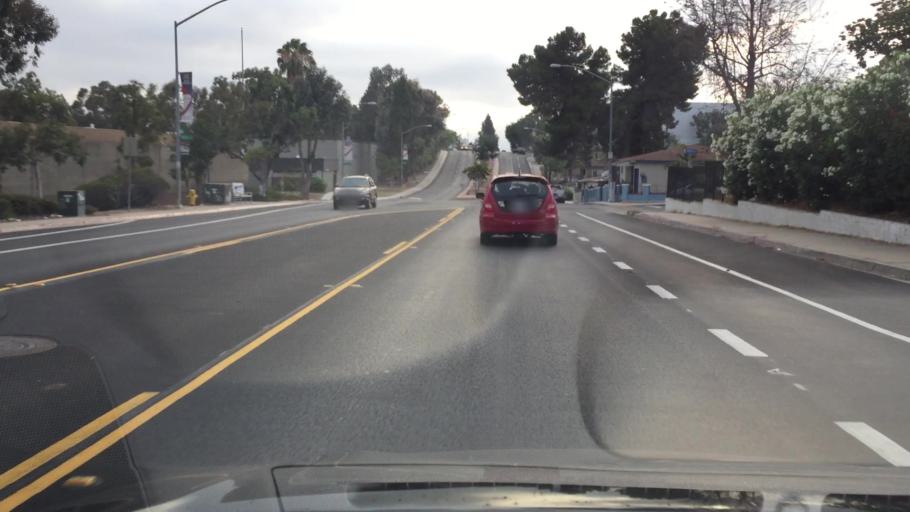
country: US
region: California
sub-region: San Diego County
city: National City
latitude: 32.7115
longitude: -117.1082
